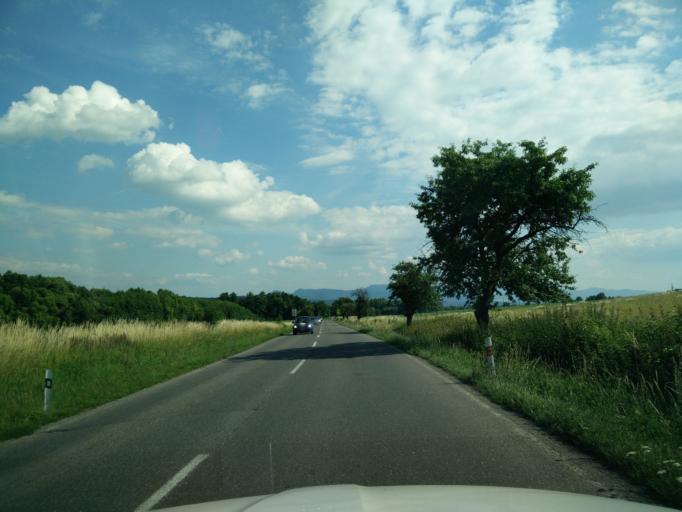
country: SK
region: Nitriansky
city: Prievidza
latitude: 48.8595
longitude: 18.6412
